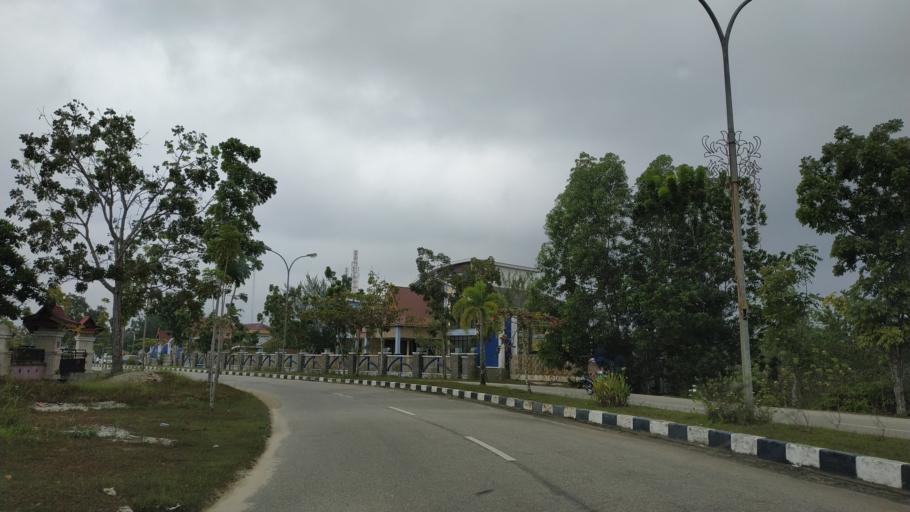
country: ID
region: Riau
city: Pangkalanbunut
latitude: 0.3855
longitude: 101.8245
